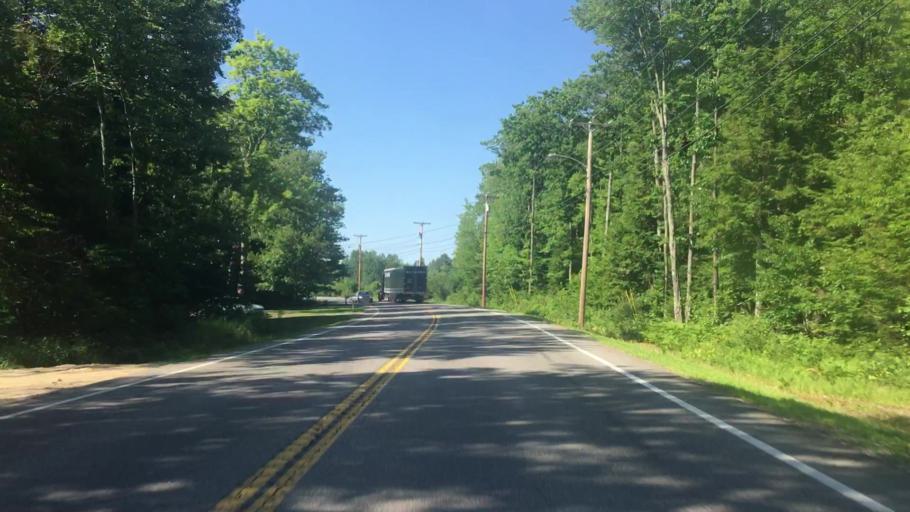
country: US
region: Maine
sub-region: York County
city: Dayton
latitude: 43.5607
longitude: -70.4984
